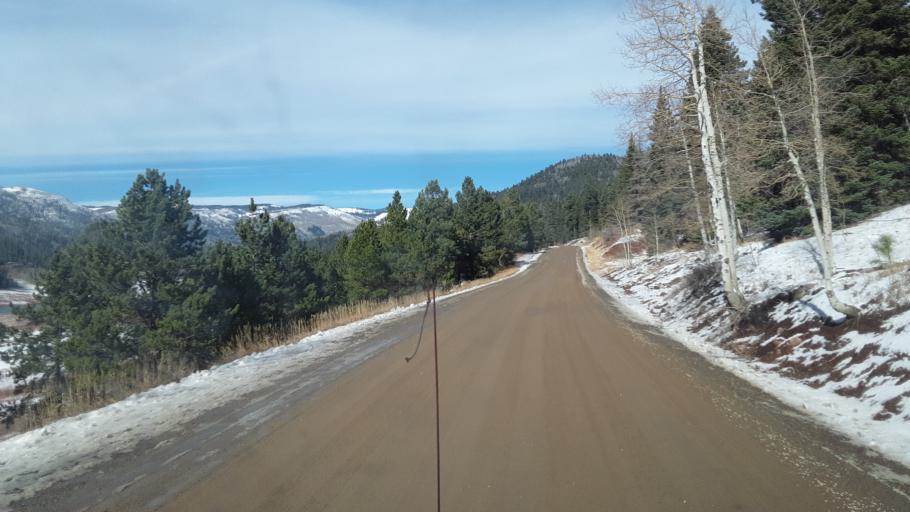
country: US
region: Colorado
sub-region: La Plata County
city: Bayfield
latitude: 37.4008
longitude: -107.6594
